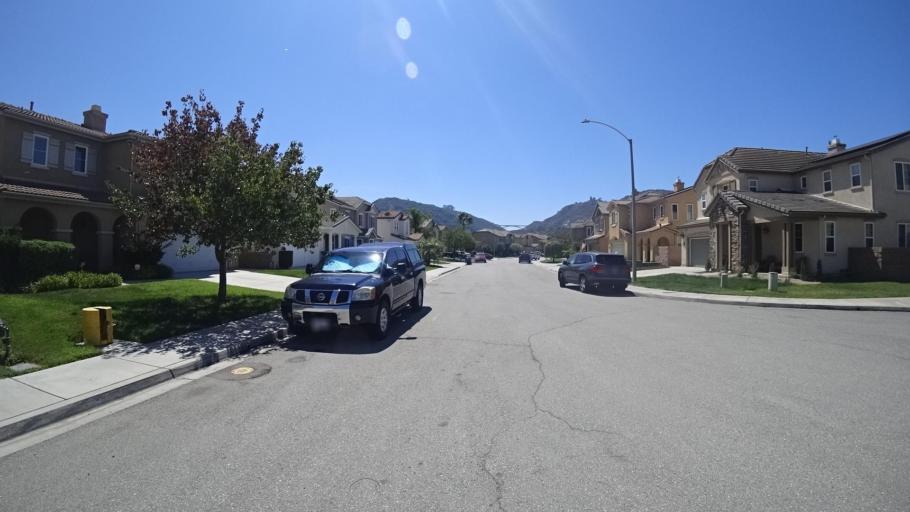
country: US
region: California
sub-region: San Diego County
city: Bonsall
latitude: 33.3228
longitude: -117.1502
